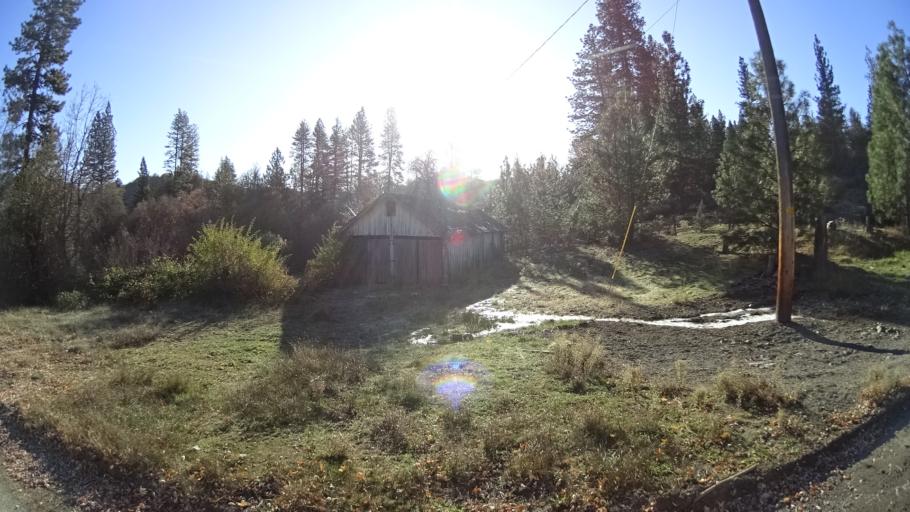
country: US
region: Oregon
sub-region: Jackson County
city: Ashland
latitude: 41.9768
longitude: -122.6332
